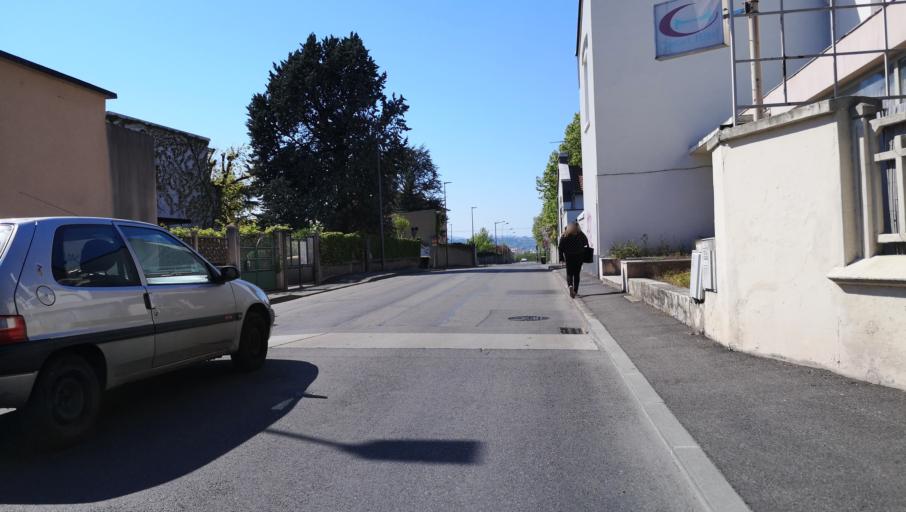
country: FR
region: Rhone-Alpes
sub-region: Departement du Rhone
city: Bron
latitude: 45.7349
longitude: 4.8913
